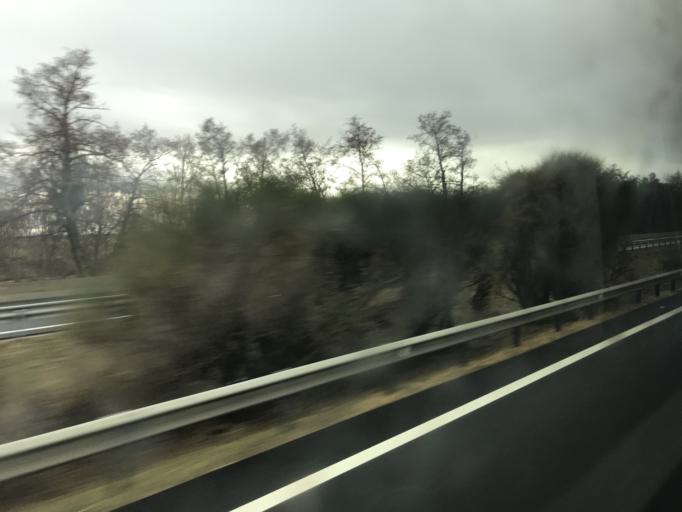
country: ES
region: Castille and Leon
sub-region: Provincia de Valladolid
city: Cubillas de Santa Marta
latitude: 41.7959
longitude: -4.5980
